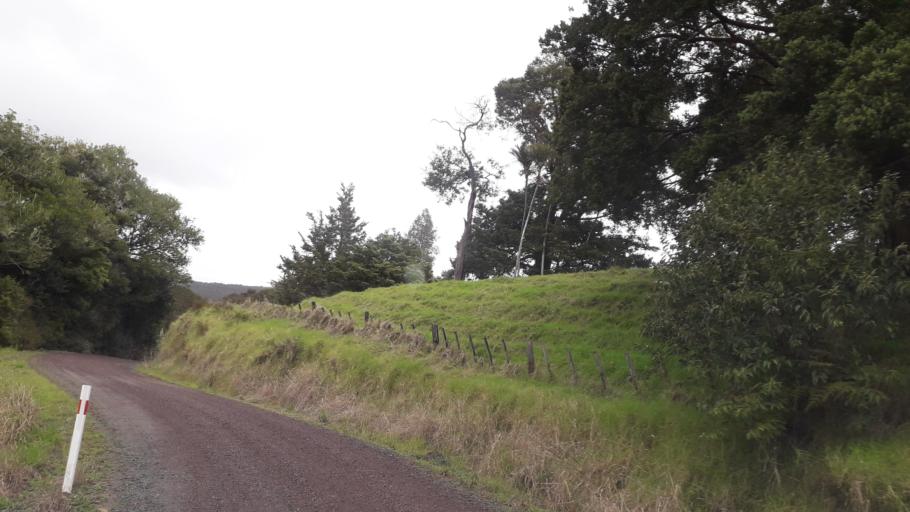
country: NZ
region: Northland
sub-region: Far North District
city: Waimate North
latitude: -35.3133
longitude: 173.5653
